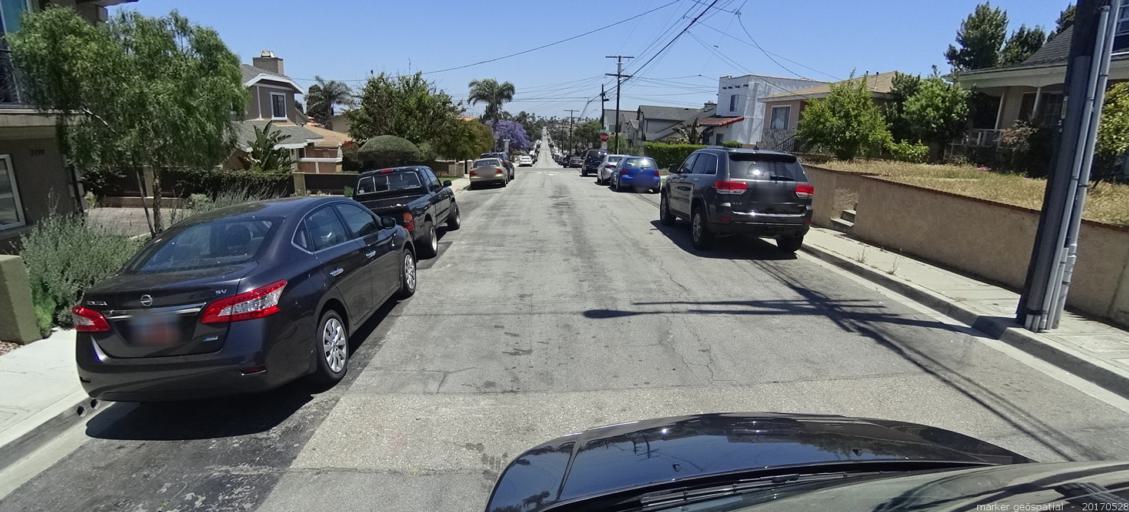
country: US
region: California
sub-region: Los Angeles County
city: Redondo Beach
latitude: 33.8680
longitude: -118.3733
